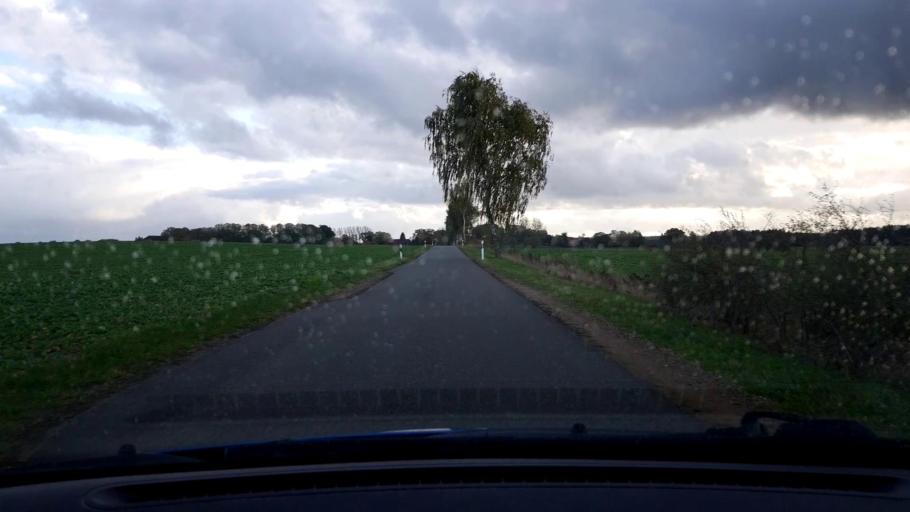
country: DE
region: Lower Saxony
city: Reinstorf
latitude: 53.2585
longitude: 10.5645
